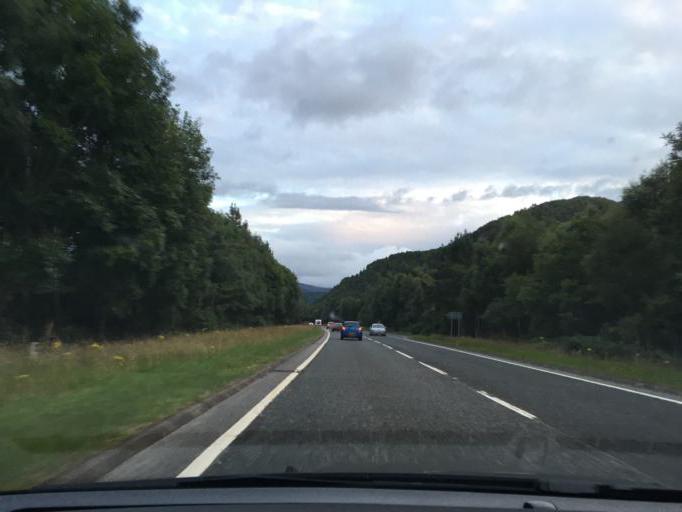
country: GB
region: Scotland
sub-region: Highland
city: Aviemore
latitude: 57.1910
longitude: -3.8370
